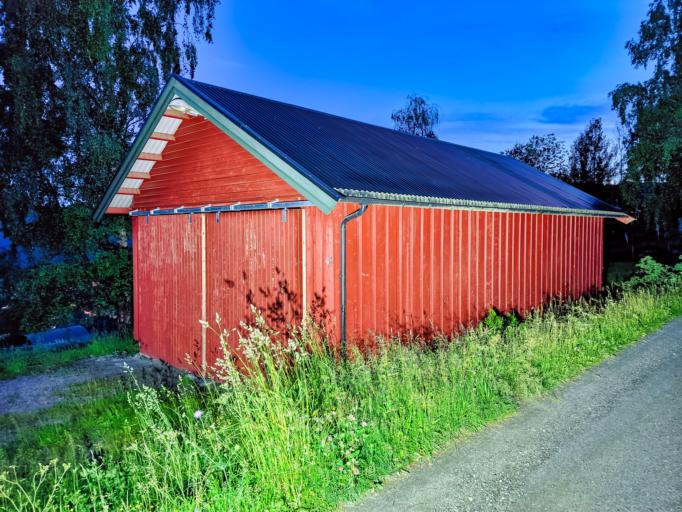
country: NO
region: Buskerud
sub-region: Gol
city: Gol
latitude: 60.7149
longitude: 8.9473
